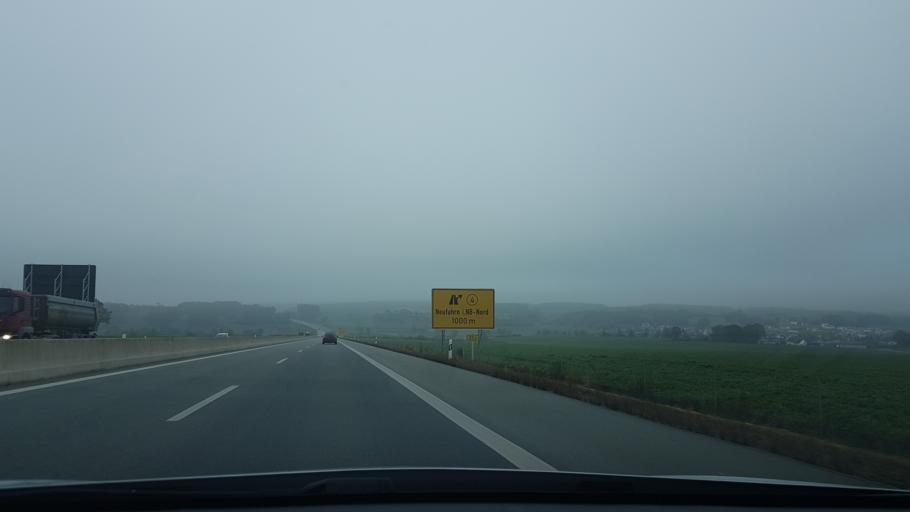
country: DE
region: Bavaria
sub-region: Lower Bavaria
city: Ergoldsbach
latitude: 48.7200
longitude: 12.1663
